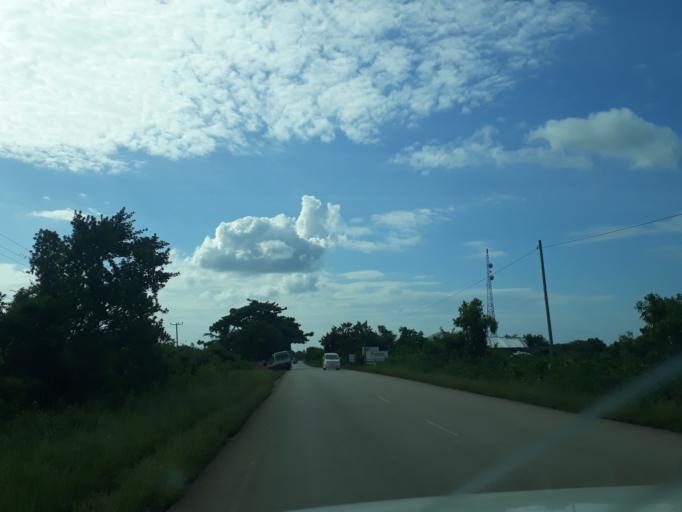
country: TZ
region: Zanzibar North
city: Nungwi
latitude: -5.7580
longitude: 39.3014
